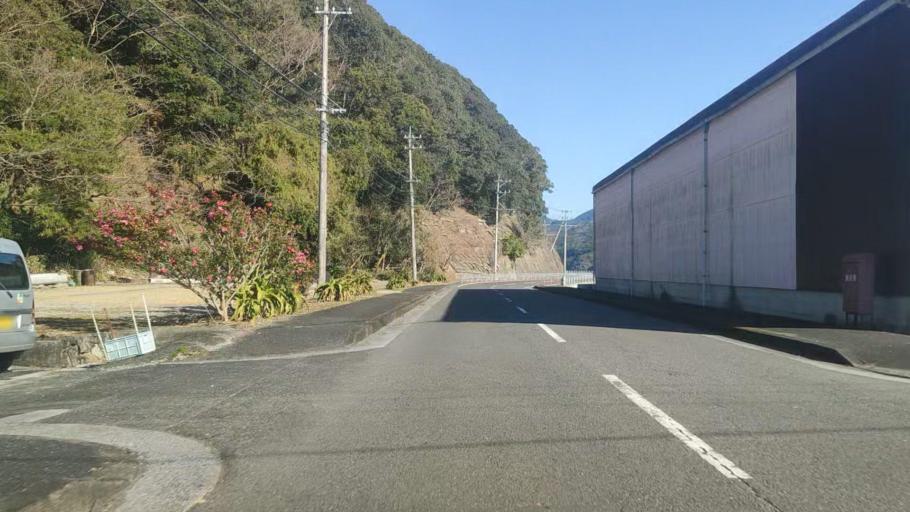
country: JP
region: Oita
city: Saiki
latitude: 32.7932
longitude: 131.8853
